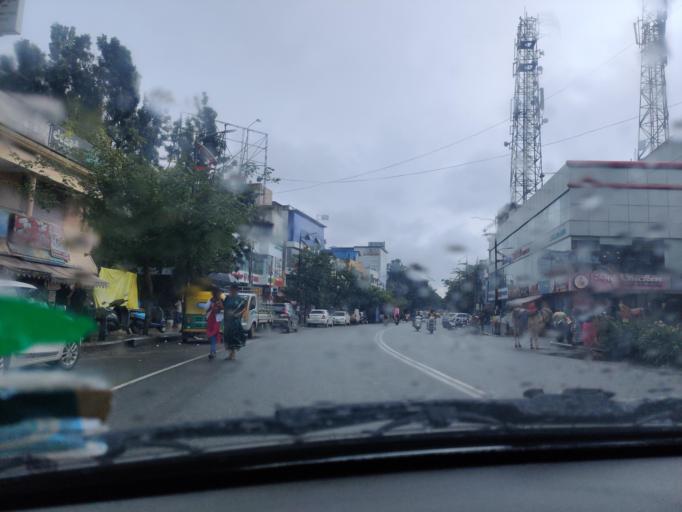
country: IN
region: Karnataka
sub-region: Bangalore Urban
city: Bangalore
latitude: 13.0200
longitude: 77.6370
